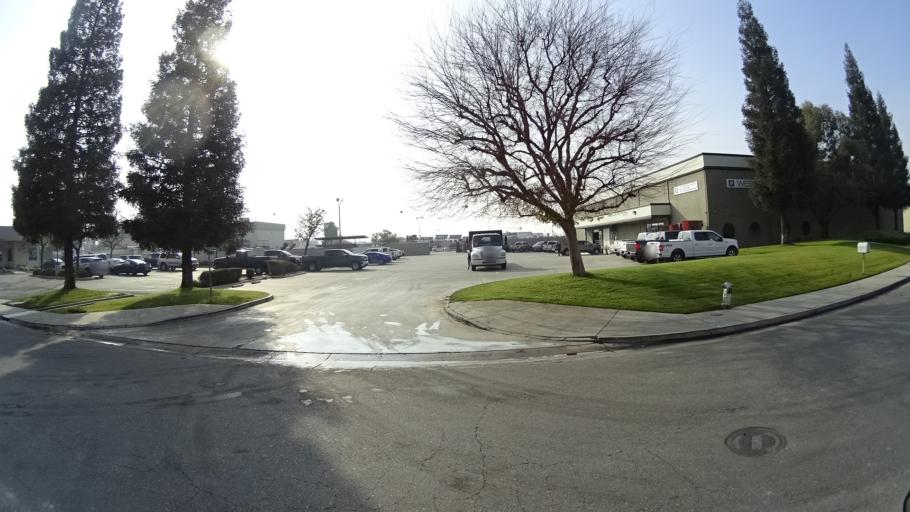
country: US
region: California
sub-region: Kern County
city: Oildale
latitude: 35.3988
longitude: -119.0400
